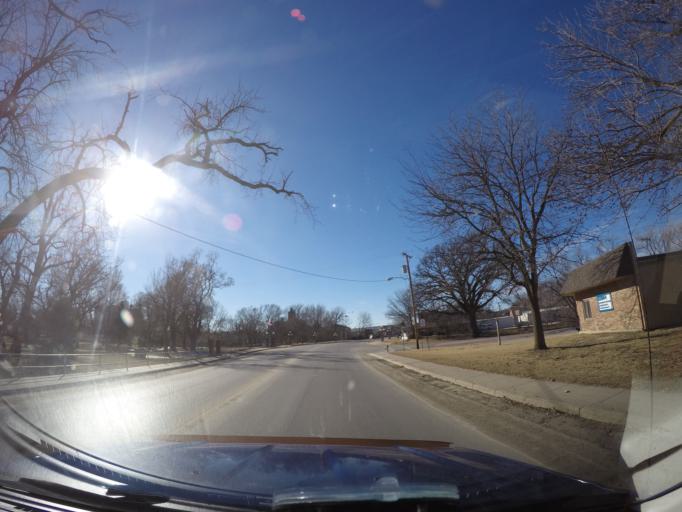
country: US
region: Kansas
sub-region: Marion County
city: Marion
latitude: 38.3484
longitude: -97.0168
